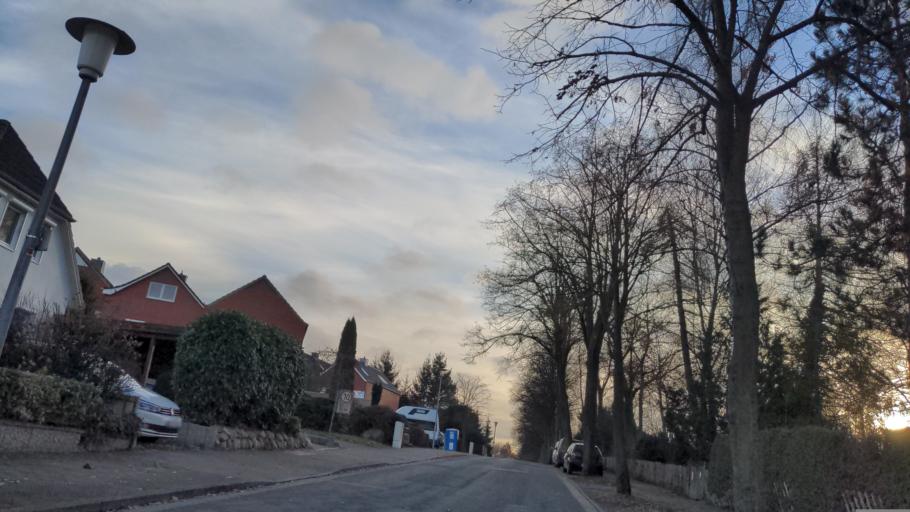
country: DE
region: Schleswig-Holstein
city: Neustadt in Holstein
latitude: 54.1079
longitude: 10.8264
